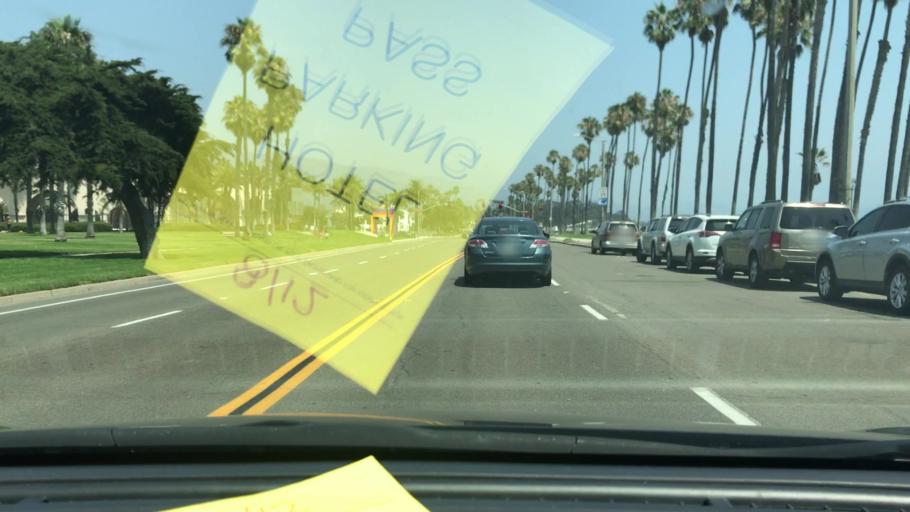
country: US
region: California
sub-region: Santa Barbara County
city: Santa Barbara
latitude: 34.4158
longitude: -119.6771
